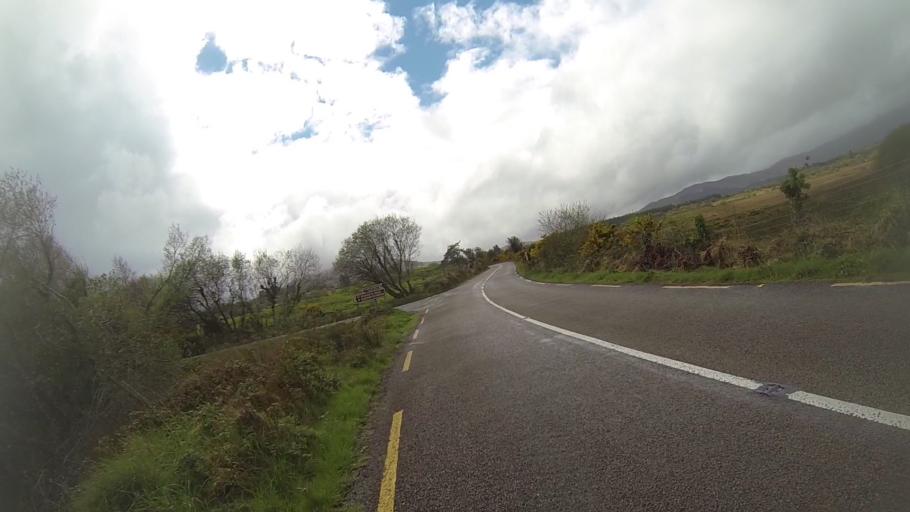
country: IE
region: Munster
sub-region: Ciarrai
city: Kenmare
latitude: 51.8886
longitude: -9.7696
